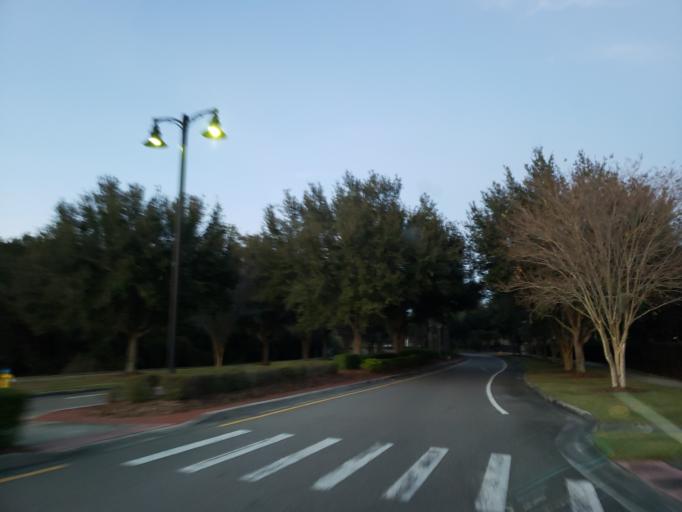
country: US
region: Florida
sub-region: Hillsborough County
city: Bloomingdale
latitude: 27.8517
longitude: -82.2606
